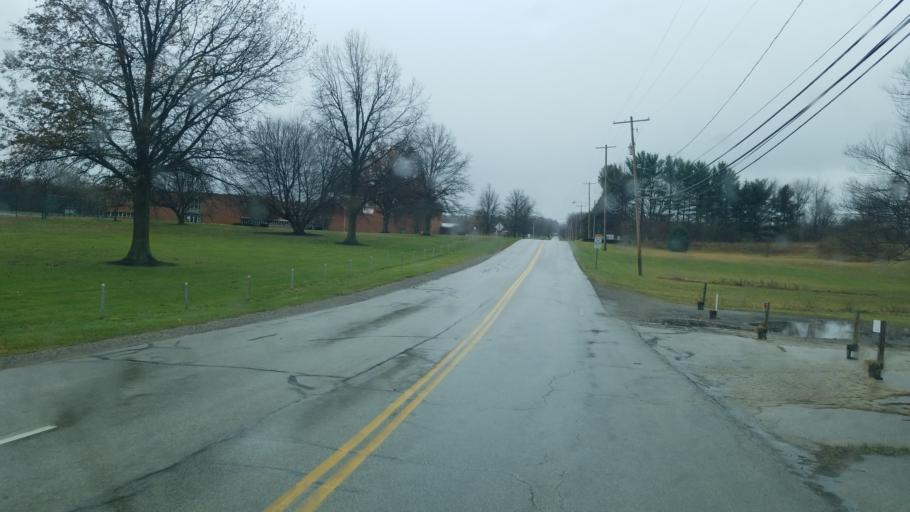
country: US
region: Ohio
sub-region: Ashtabula County
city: Edgewood
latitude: 41.8887
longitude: -80.7316
